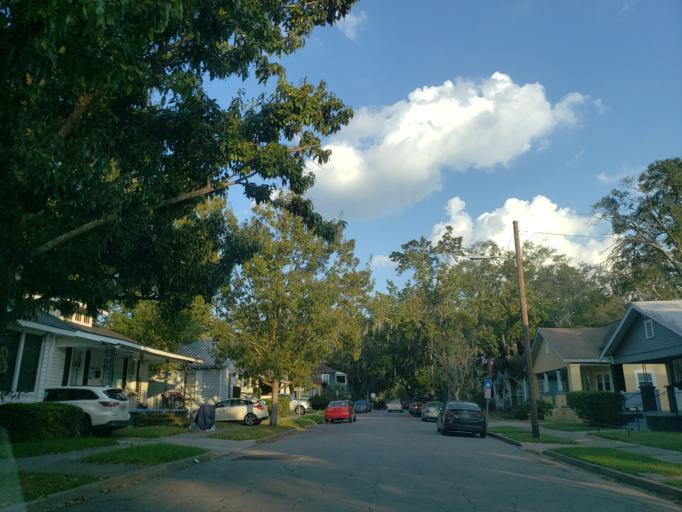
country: US
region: Georgia
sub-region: Chatham County
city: Savannah
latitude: 32.0561
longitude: -81.0835
